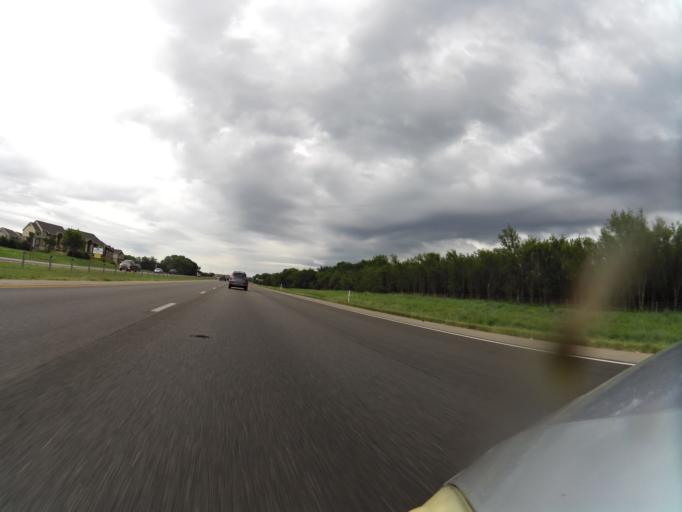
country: US
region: Kansas
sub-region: Sedgwick County
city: Bellaire
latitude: 37.7455
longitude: -97.2754
